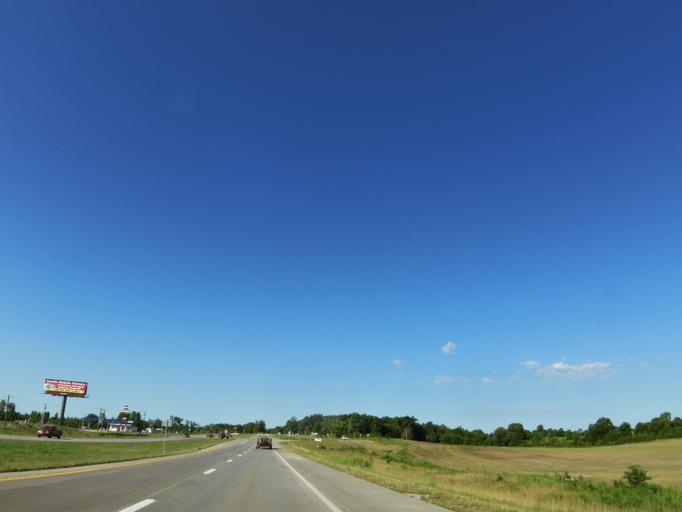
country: US
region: Missouri
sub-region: Butler County
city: Poplar Bluff
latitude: 36.6893
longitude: -90.4833
